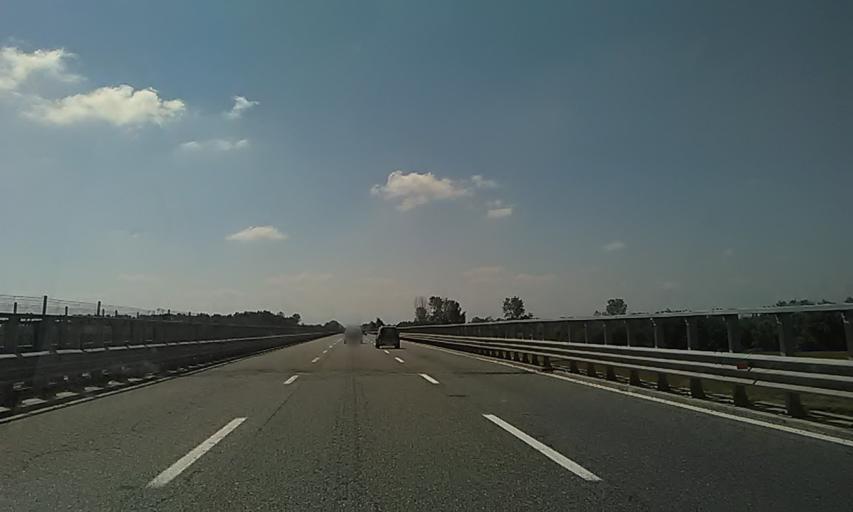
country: IT
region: Piedmont
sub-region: Provincia di Alessandria
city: Castellazzo Bormida
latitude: 44.8675
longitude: 8.5775
